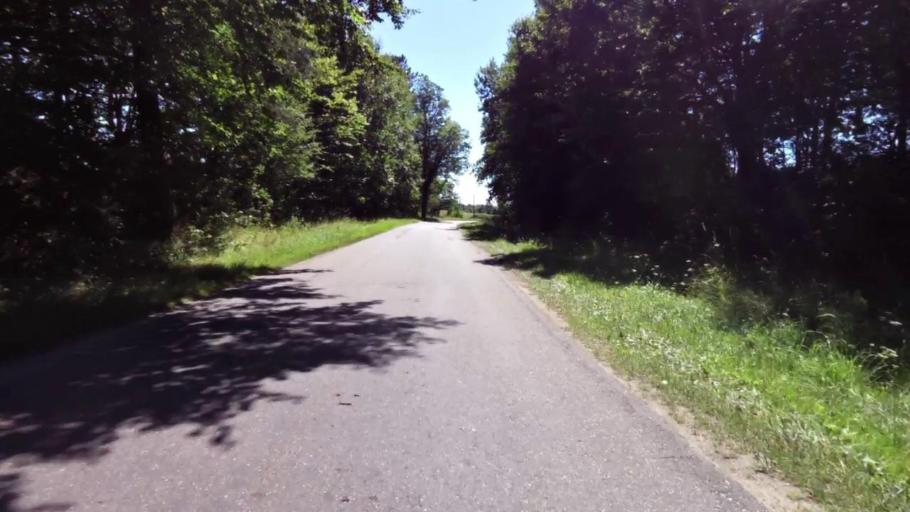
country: PL
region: West Pomeranian Voivodeship
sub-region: Powiat szczecinecki
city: Bialy Bor
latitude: 53.9298
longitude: 16.8519
